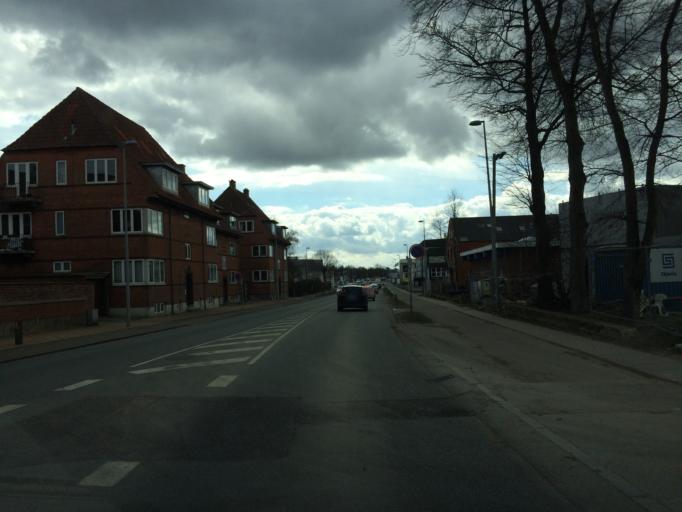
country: DK
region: South Denmark
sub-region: Odense Kommune
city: Odense
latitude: 55.3977
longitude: 10.3671
